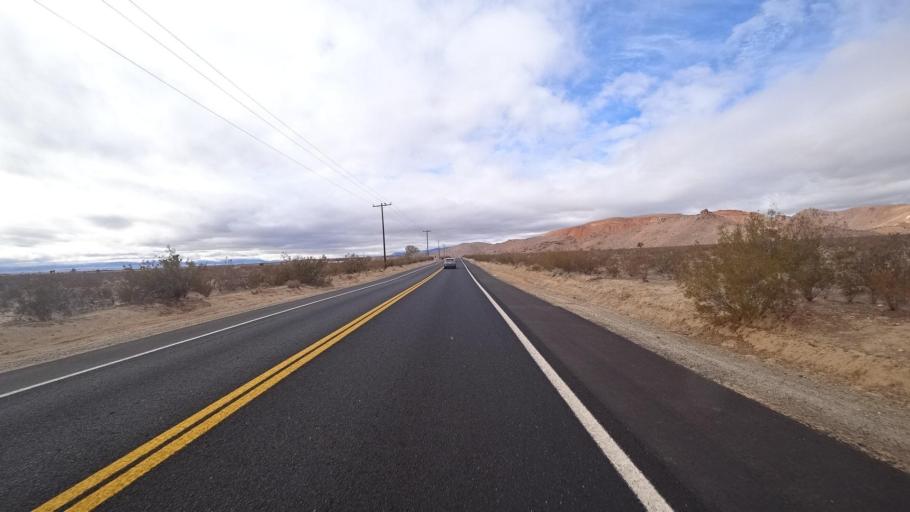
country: US
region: California
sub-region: Kern County
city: Rosamond
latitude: 34.9510
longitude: -118.2587
